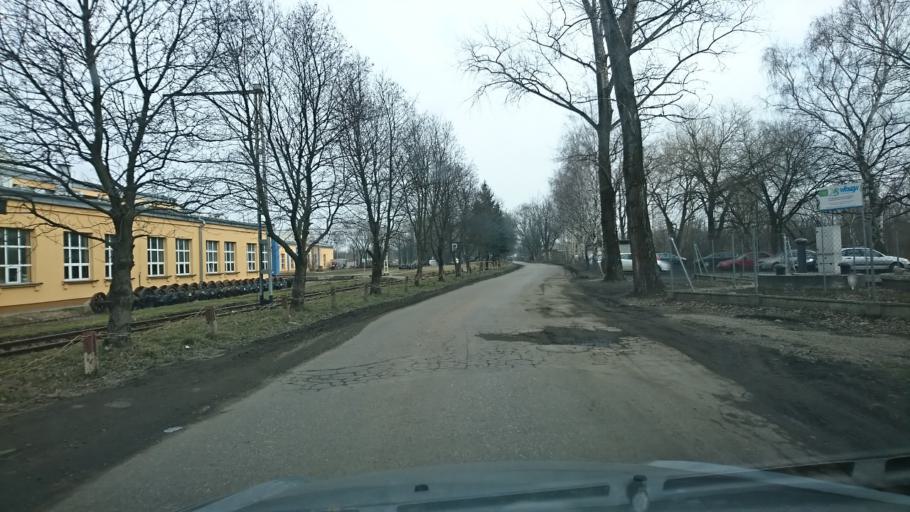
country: PL
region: Lesser Poland Voivodeship
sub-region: Powiat wielicki
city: Czarnochowice
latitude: 50.0221
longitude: 20.0325
